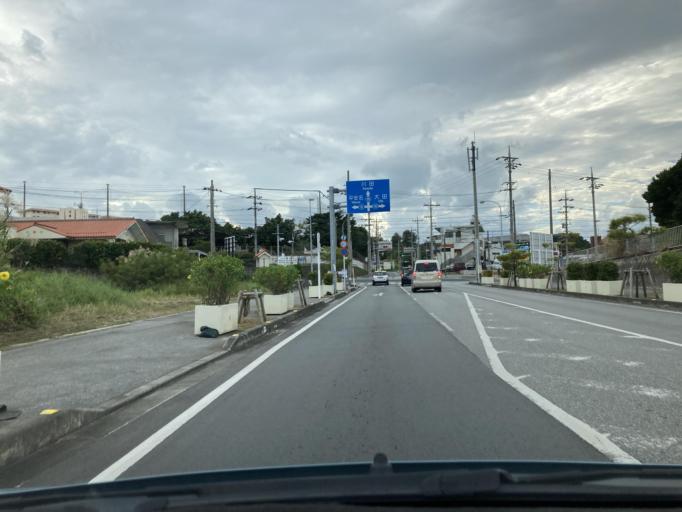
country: JP
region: Okinawa
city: Katsuren-haebaru
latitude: 26.3303
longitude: 127.8847
